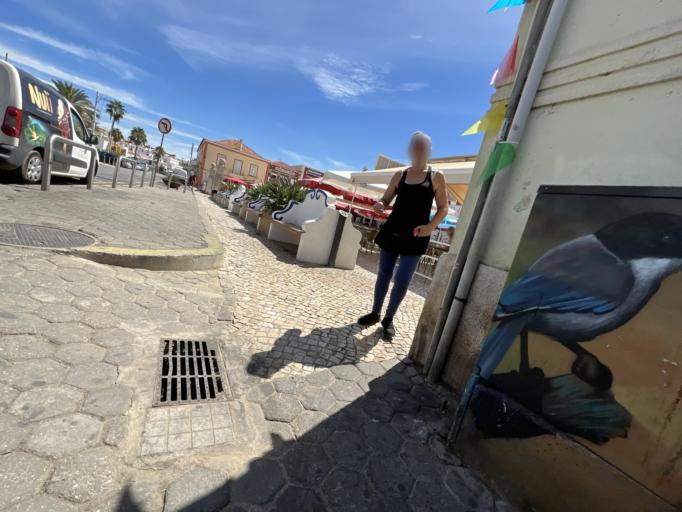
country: PT
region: Faro
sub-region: Portimao
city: Portimao
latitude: 37.1248
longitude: -8.5200
